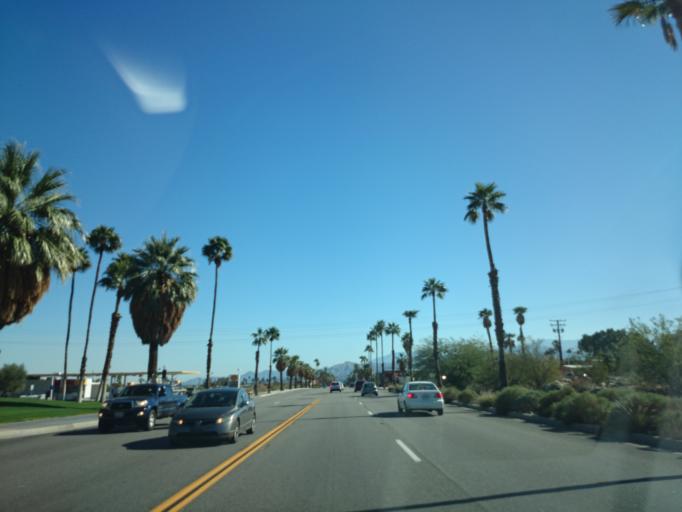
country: US
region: California
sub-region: Riverside County
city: Palm Springs
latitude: 33.8567
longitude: -116.5560
